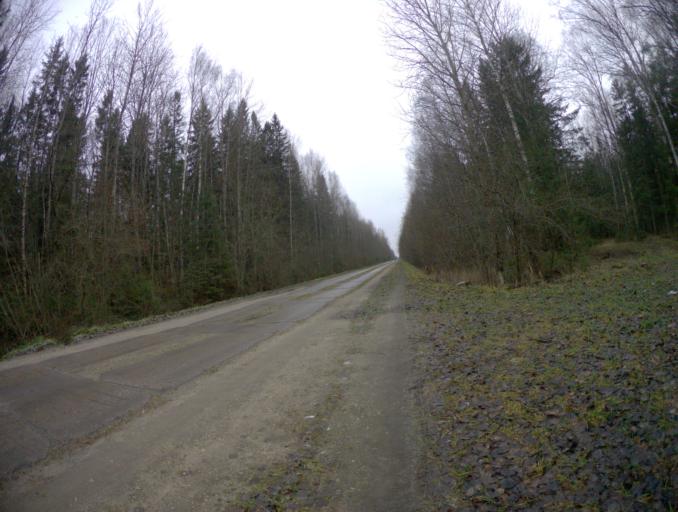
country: RU
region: Vladimir
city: Kommunar
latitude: 56.0352
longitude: 40.5164
